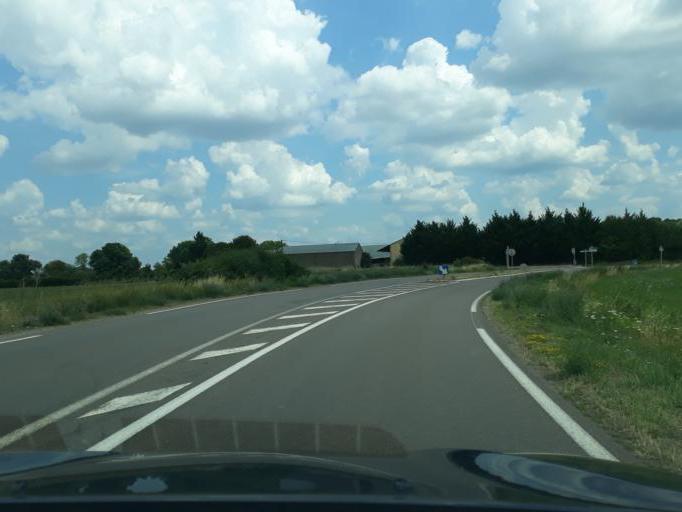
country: FR
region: Centre
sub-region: Departement du Cher
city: Nerondes
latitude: 47.0006
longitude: 2.8014
